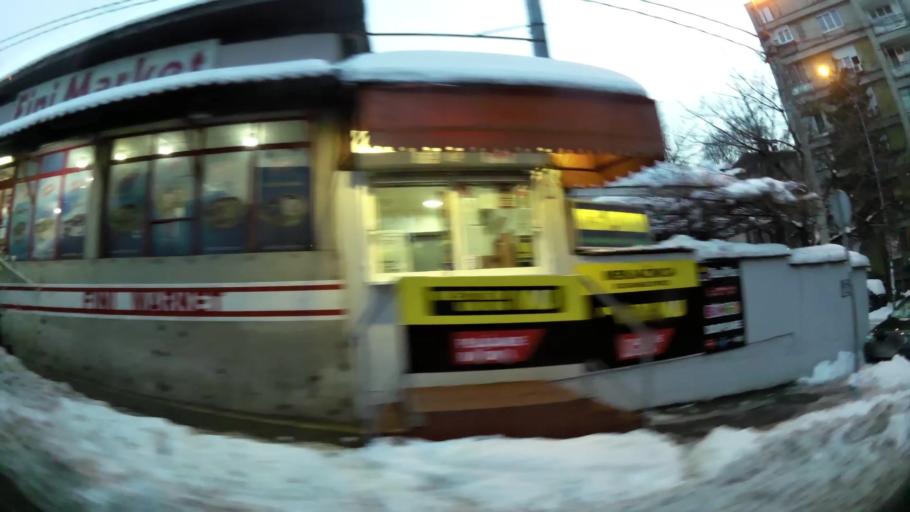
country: RS
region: Central Serbia
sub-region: Belgrade
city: Palilula
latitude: 44.7980
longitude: 20.5067
